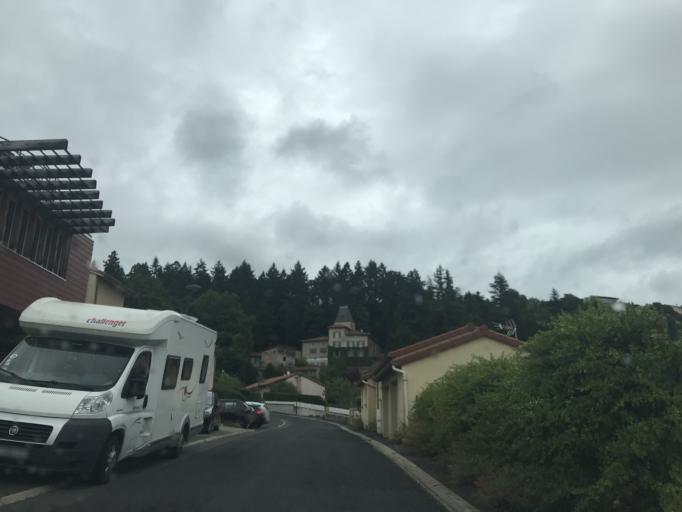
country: FR
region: Auvergne
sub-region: Departement de la Haute-Loire
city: Le Puy-en-Velay
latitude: 45.0550
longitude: 3.8786
